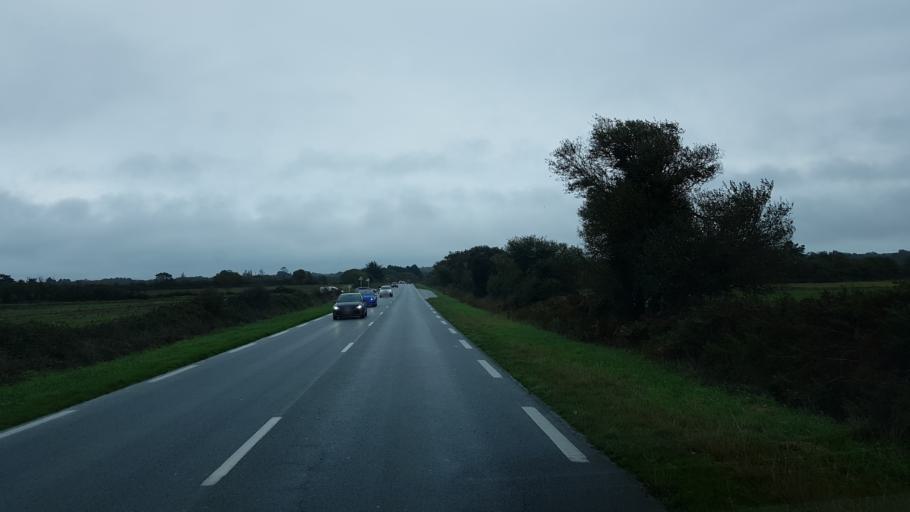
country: FR
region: Brittany
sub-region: Departement du Morbihan
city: Saint-Gildas-de-Rhuys
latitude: 47.5313
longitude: -2.8341
